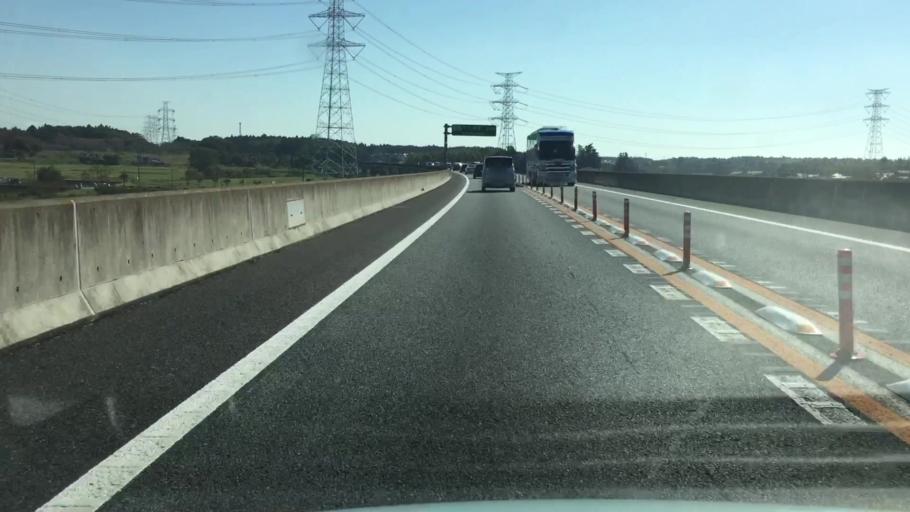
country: JP
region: Ibaraki
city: Ushiku
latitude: 35.9950
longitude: 140.1564
